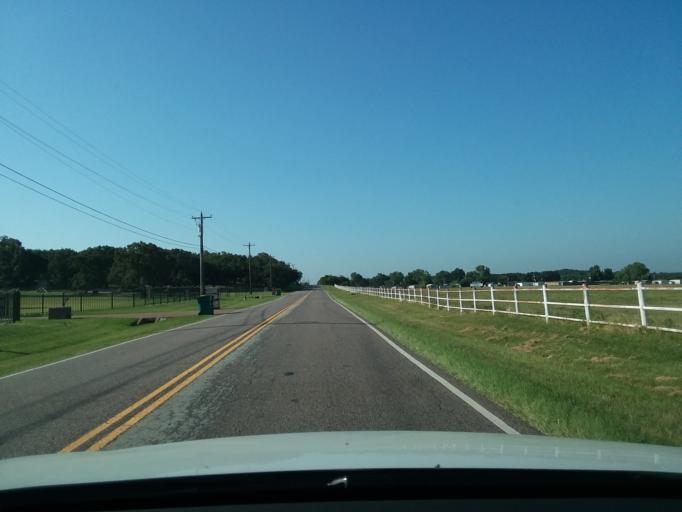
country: US
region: Texas
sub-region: Denton County
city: Bartonville
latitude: 33.0529
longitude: -97.1290
